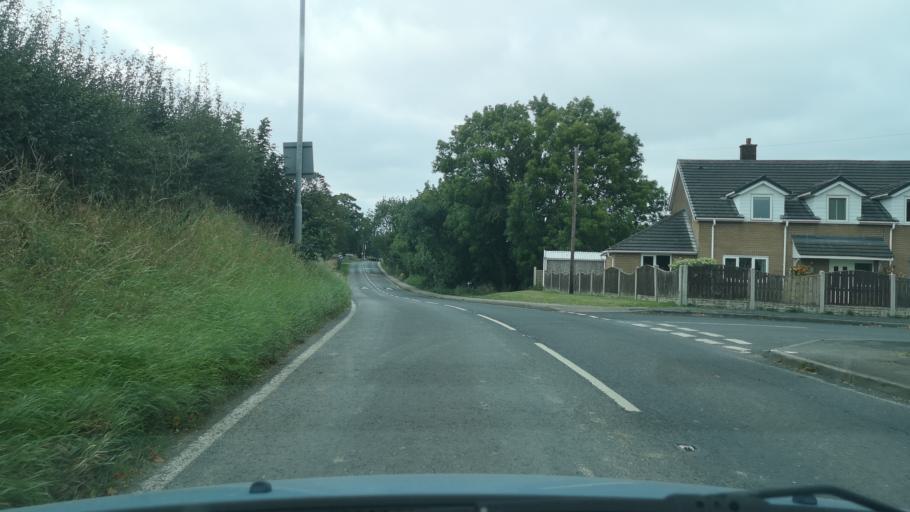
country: GB
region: England
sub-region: City and Borough of Wakefield
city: Badsworth
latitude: 53.6341
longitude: -1.2901
